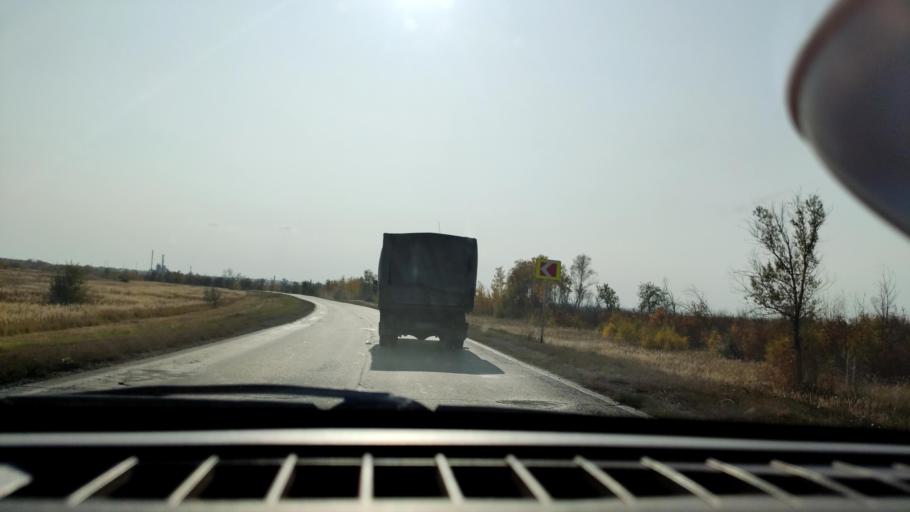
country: RU
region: Samara
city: Smyshlyayevka
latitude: 53.1089
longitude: 50.3526
